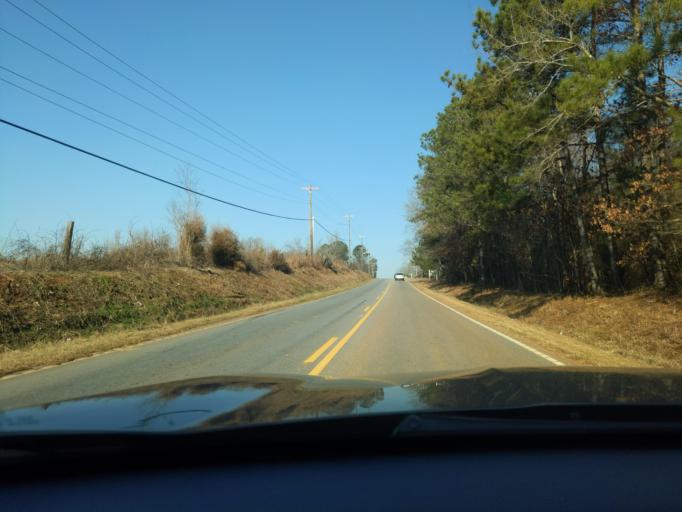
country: US
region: South Carolina
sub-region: Greenwood County
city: Greenwood
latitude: 34.1934
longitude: -82.1266
